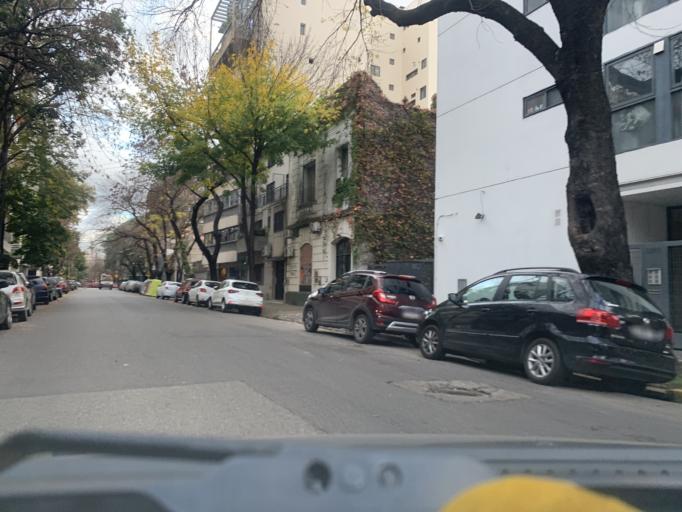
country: AR
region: Buenos Aires F.D.
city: Colegiales
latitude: -34.5768
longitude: -58.4377
